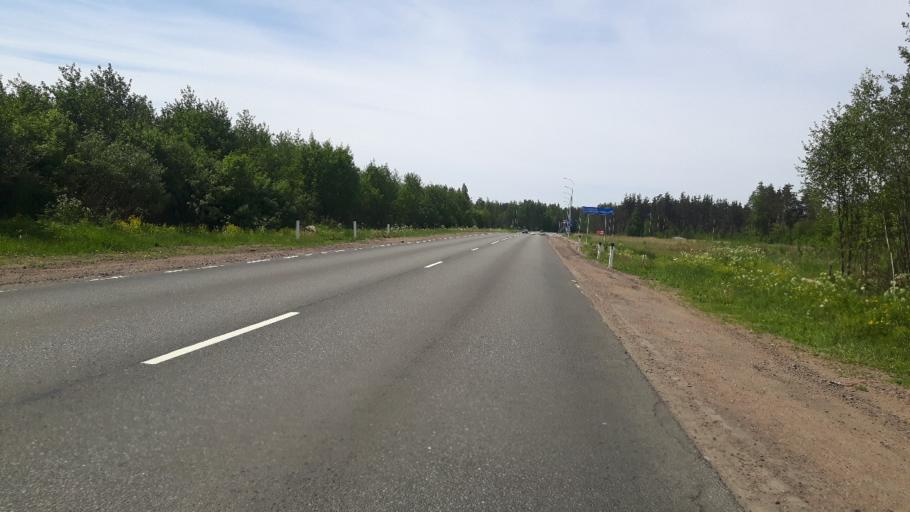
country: RU
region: Leningrad
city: Ust'-Luga
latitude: 59.6529
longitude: 28.3742
